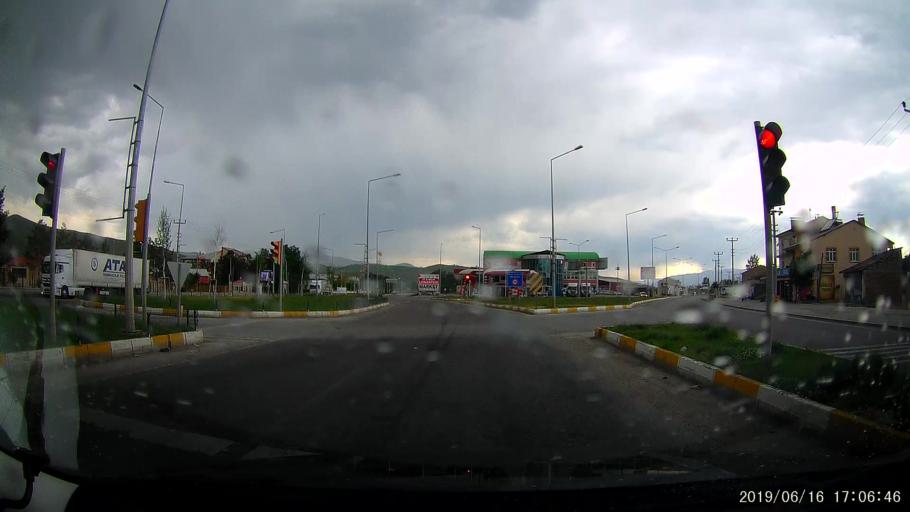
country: TR
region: Erzurum
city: Askale
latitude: 39.9187
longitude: 40.6832
